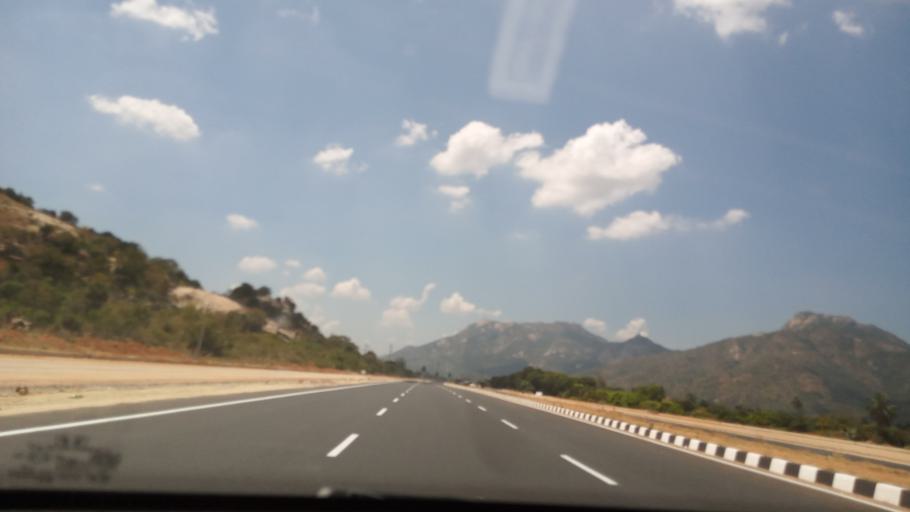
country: IN
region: Andhra Pradesh
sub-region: Chittoor
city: Narasingapuram
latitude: 13.5662
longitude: 79.2606
